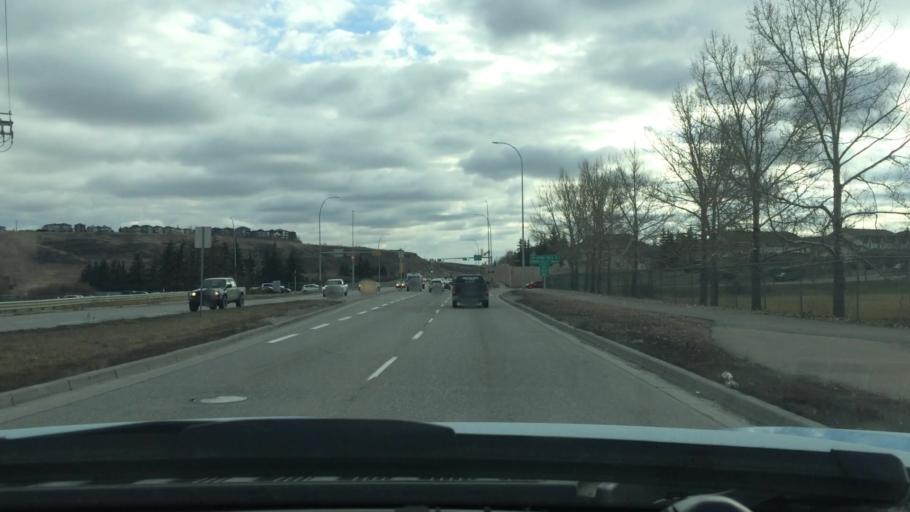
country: CA
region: Alberta
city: Calgary
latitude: 51.1542
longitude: -114.1080
